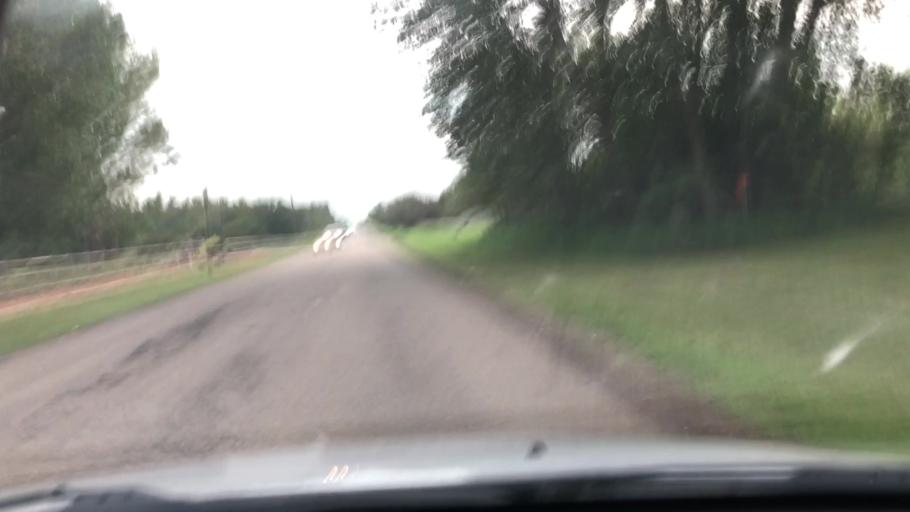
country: CA
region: Alberta
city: Devon
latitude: 53.4167
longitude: -113.6892
